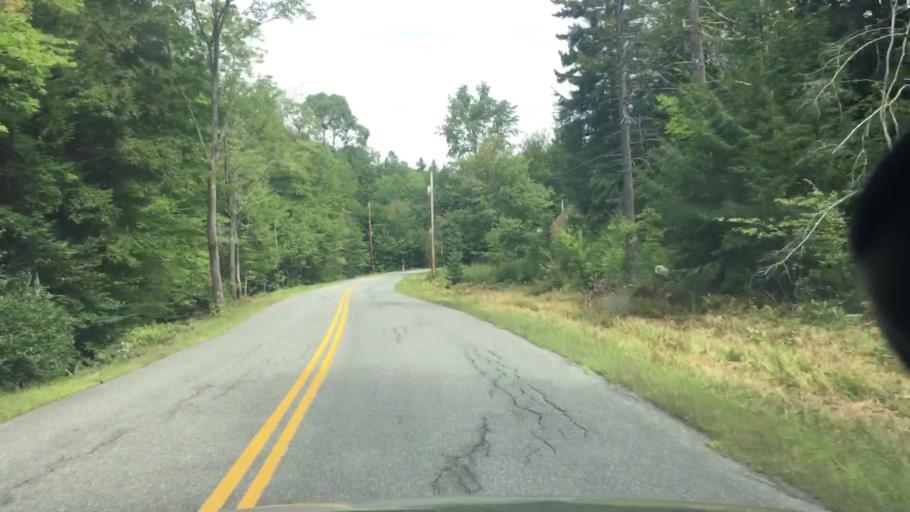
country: US
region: Vermont
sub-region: Windham County
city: Dover
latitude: 42.8023
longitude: -72.7689
